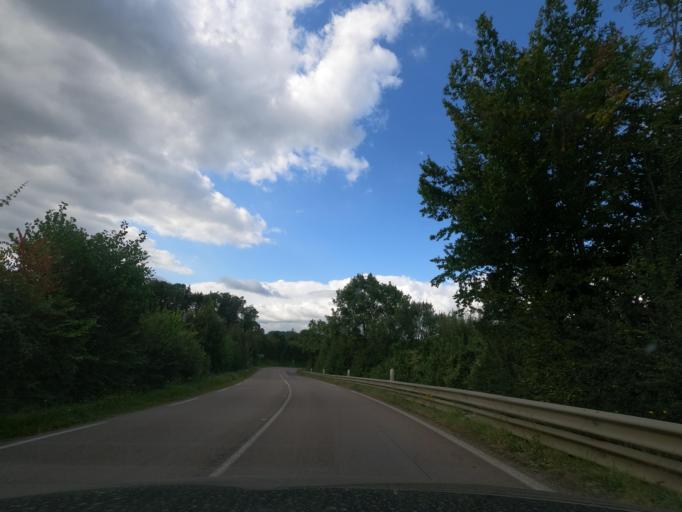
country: FR
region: Lower Normandy
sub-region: Departement de l'Orne
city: Gace
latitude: 48.8051
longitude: 0.3106
